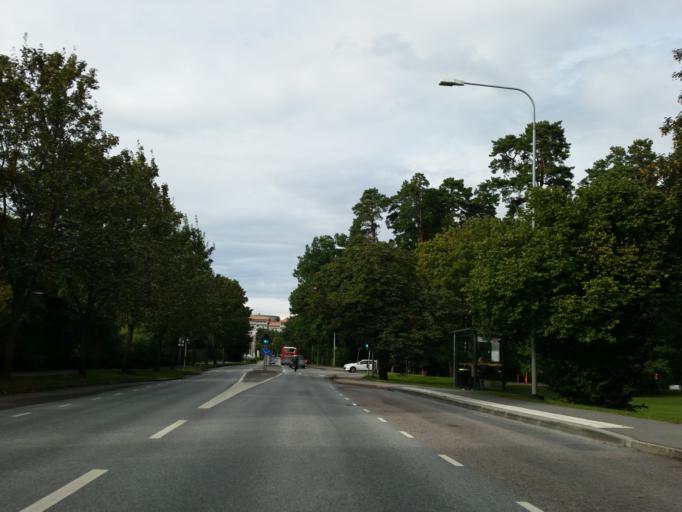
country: SE
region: Stockholm
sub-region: Sollentuna Kommun
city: Sollentuna
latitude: 59.4381
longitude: 17.9508
